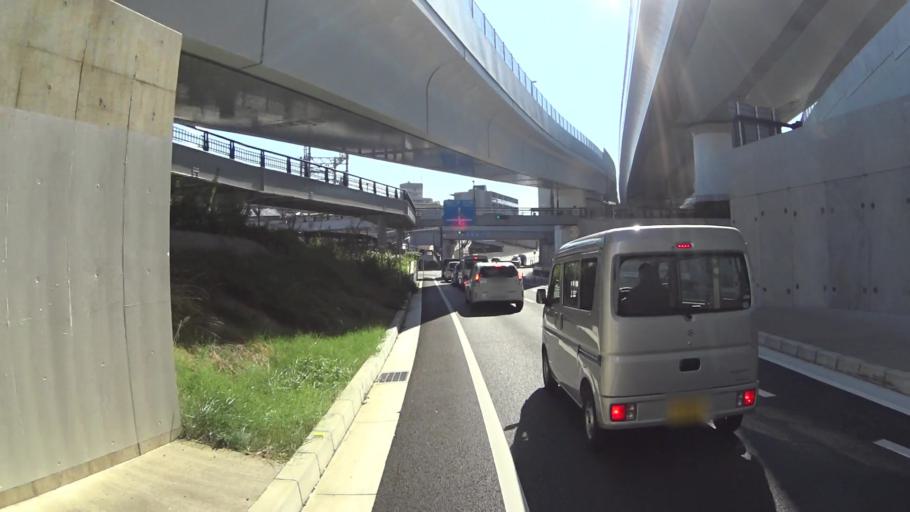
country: JP
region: Kyoto
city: Yawata
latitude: 34.9146
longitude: 135.6873
